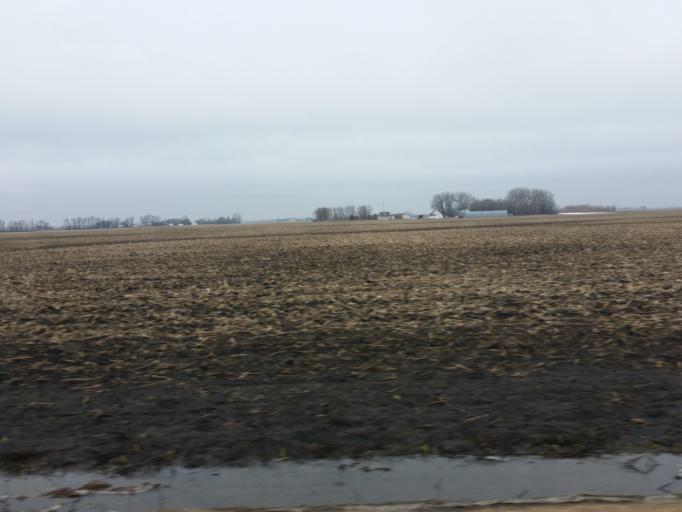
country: US
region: North Dakota
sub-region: Walsh County
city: Grafton
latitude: 48.3549
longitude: -97.2111
